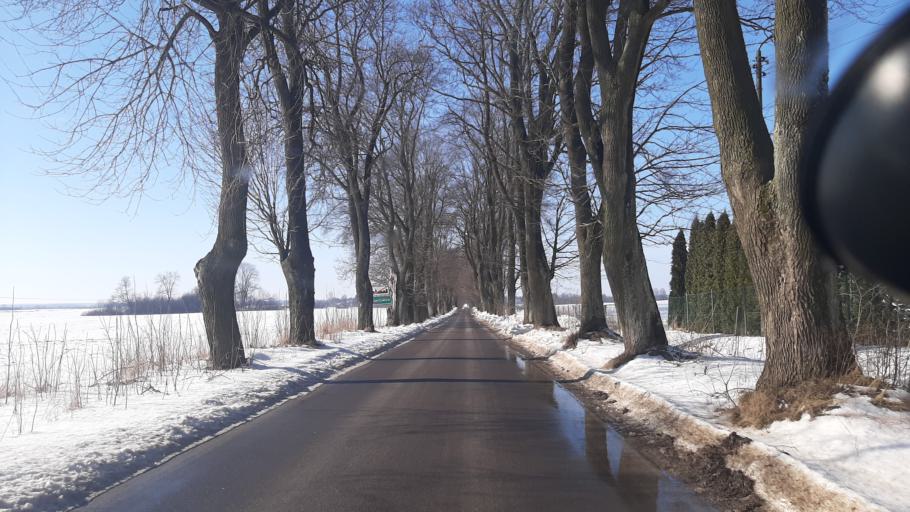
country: PL
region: Lublin Voivodeship
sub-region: Powiat pulawski
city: Naleczow
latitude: 51.3041
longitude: 22.2540
